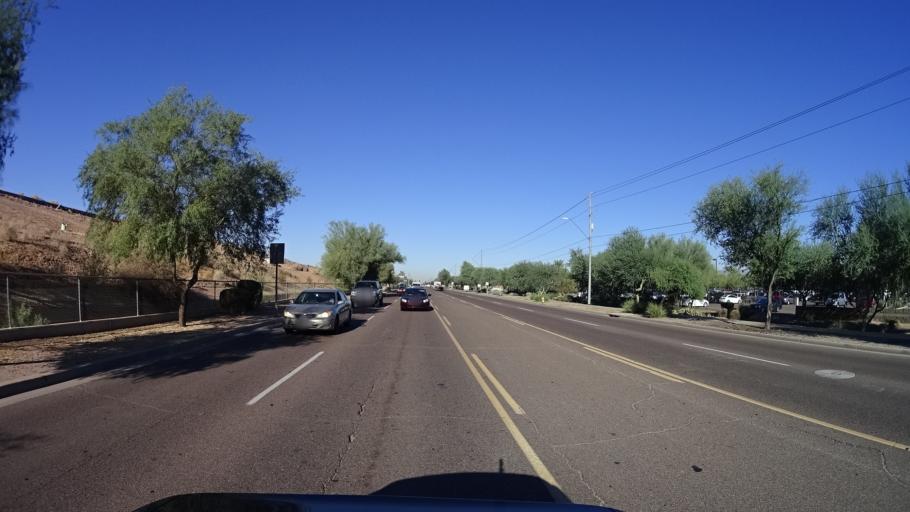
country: US
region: Arizona
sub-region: Maricopa County
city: Phoenix
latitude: 33.4224
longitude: -112.1296
